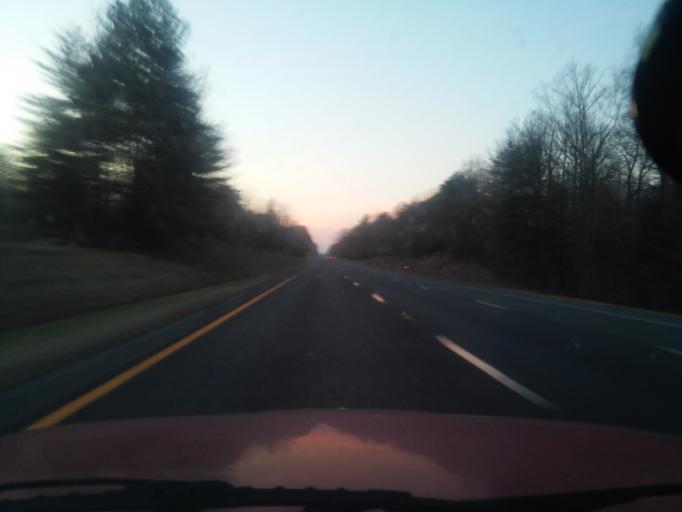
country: US
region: Virginia
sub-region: Fluvanna County
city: Palmyra
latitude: 37.9800
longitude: -78.2199
